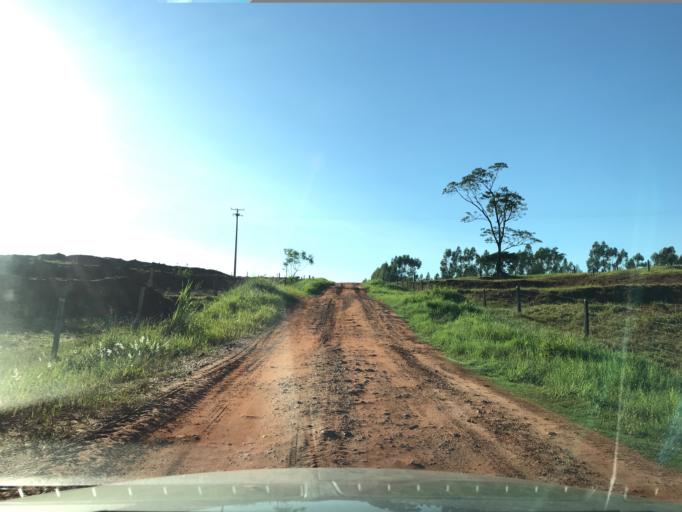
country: BR
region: Parana
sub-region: Ipora
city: Ipora
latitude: -23.9943
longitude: -53.7276
